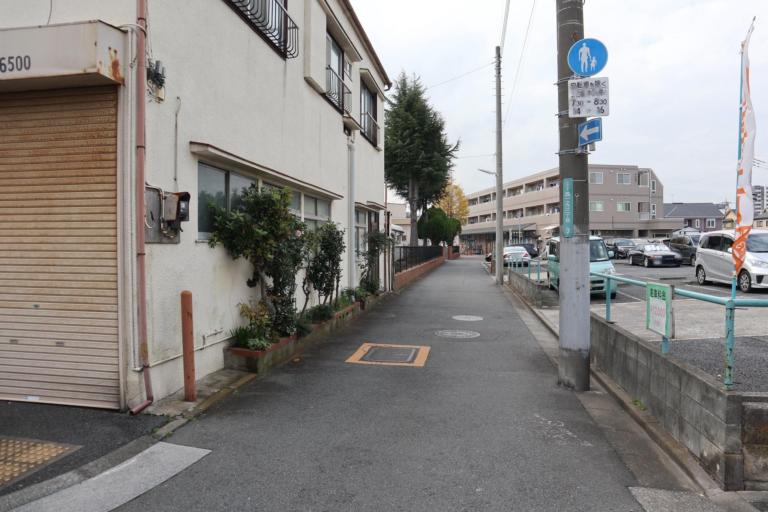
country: JP
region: Tokyo
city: Urayasu
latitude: 35.7010
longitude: 139.8797
